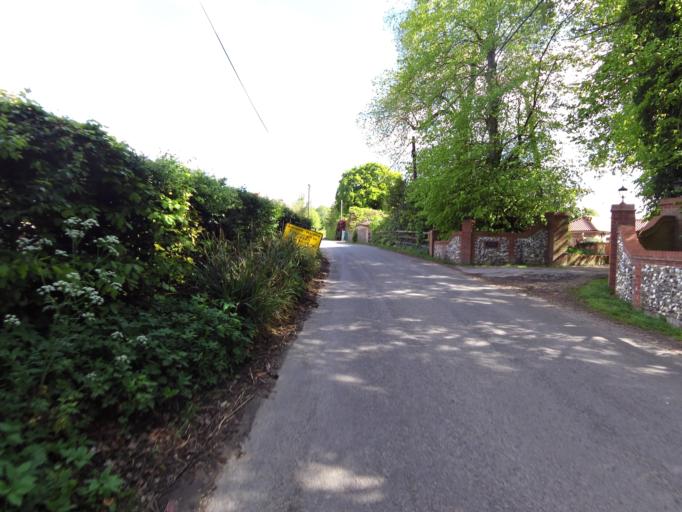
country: GB
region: England
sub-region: Suffolk
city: Thurston
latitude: 52.2477
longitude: 0.8242
